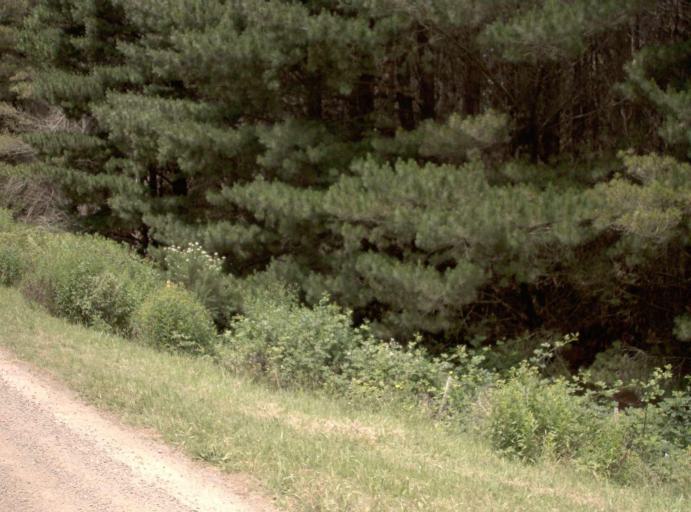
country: AU
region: Victoria
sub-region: Latrobe
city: Traralgon
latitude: -38.4079
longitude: 146.6364
